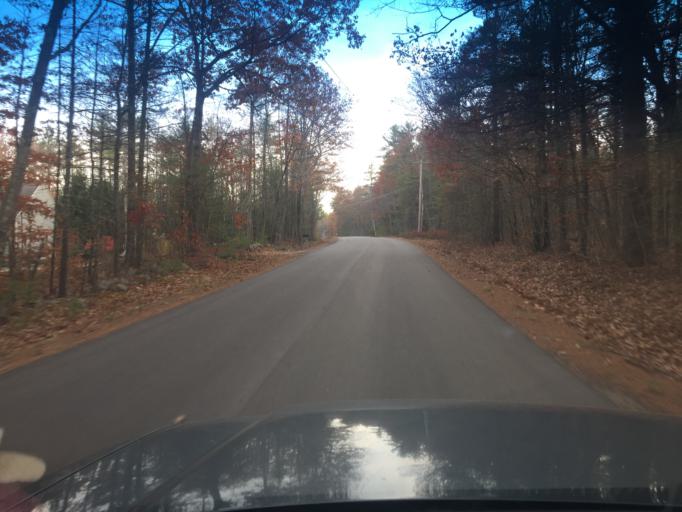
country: US
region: Maine
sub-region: York County
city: Eliot
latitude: 43.1941
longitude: -70.7483
